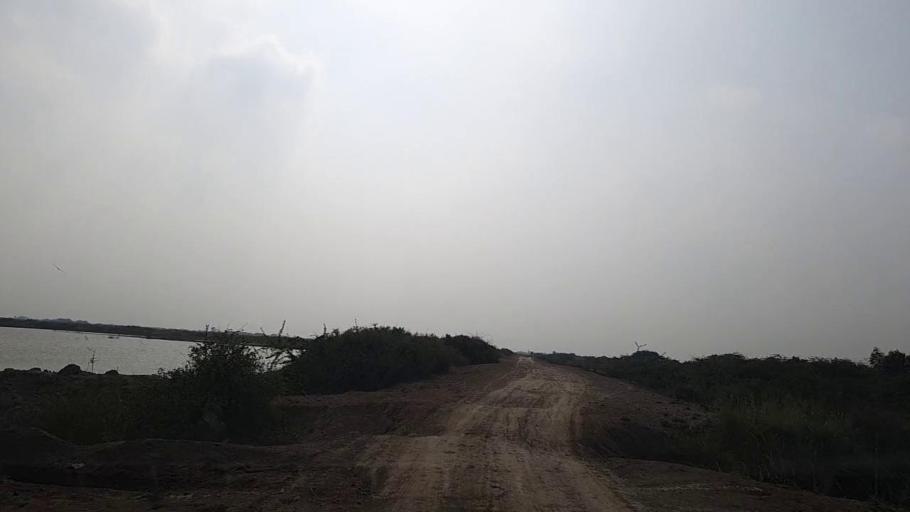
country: PK
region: Sindh
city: Gharo
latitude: 24.6754
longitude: 67.6469
